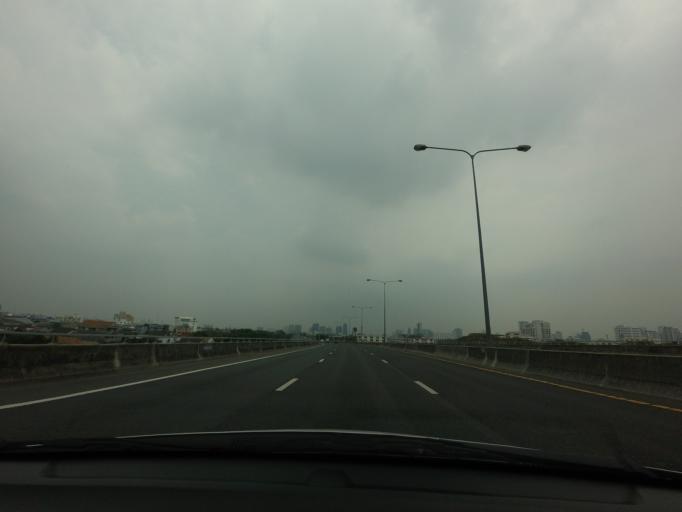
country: TH
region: Bangkok
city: Watthana
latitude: 13.7383
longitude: 100.6044
